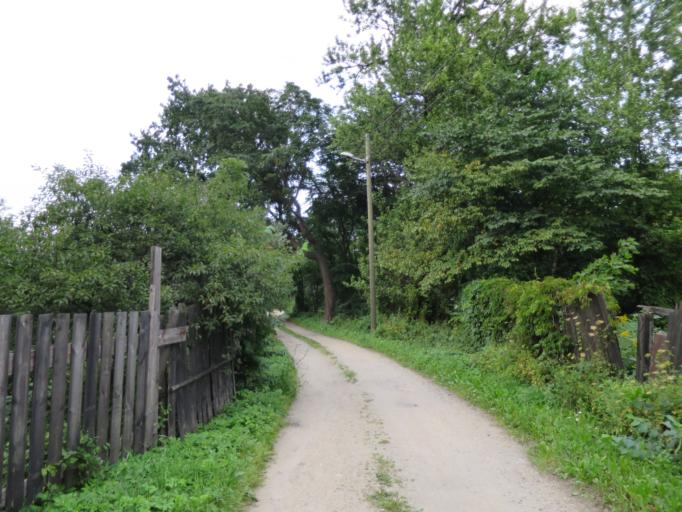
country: LV
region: Riga
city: Riga
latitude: 56.9790
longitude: 24.1000
